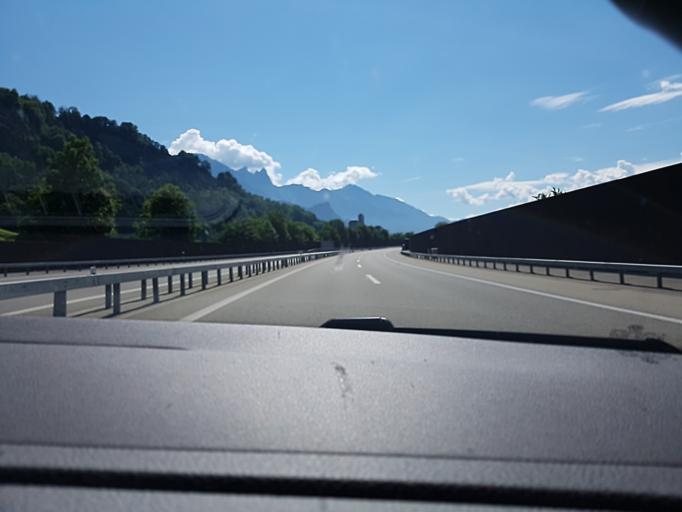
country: CH
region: Saint Gallen
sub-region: Wahlkreis Sarganserland
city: Sargans
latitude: 47.0538
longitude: 9.4220
